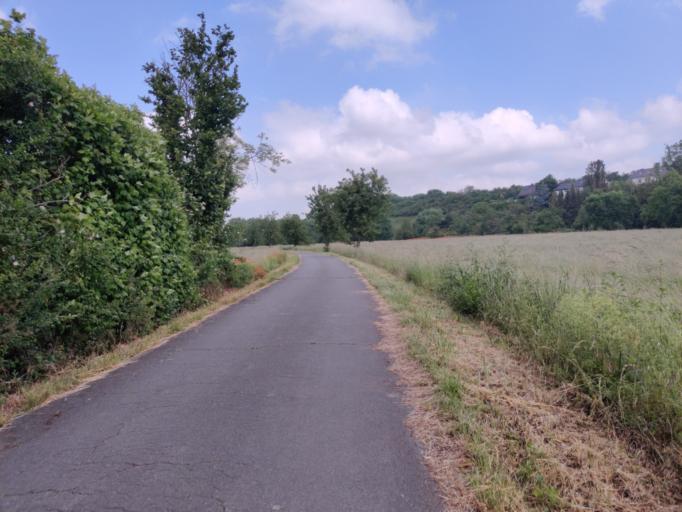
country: DE
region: Lower Saxony
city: Hildesheim
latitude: 52.1178
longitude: 9.9792
